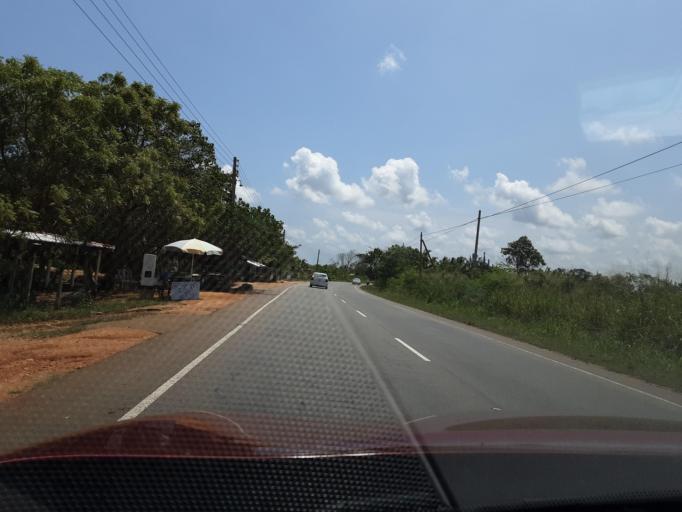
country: LK
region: Southern
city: Tangalla
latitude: 6.2162
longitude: 81.2105
